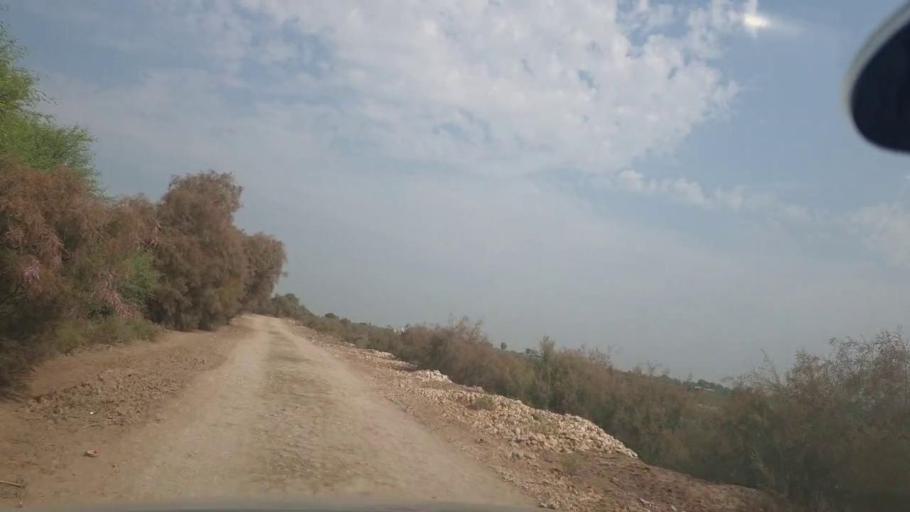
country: PK
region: Balochistan
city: Mehrabpur
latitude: 28.1083
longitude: 68.0907
